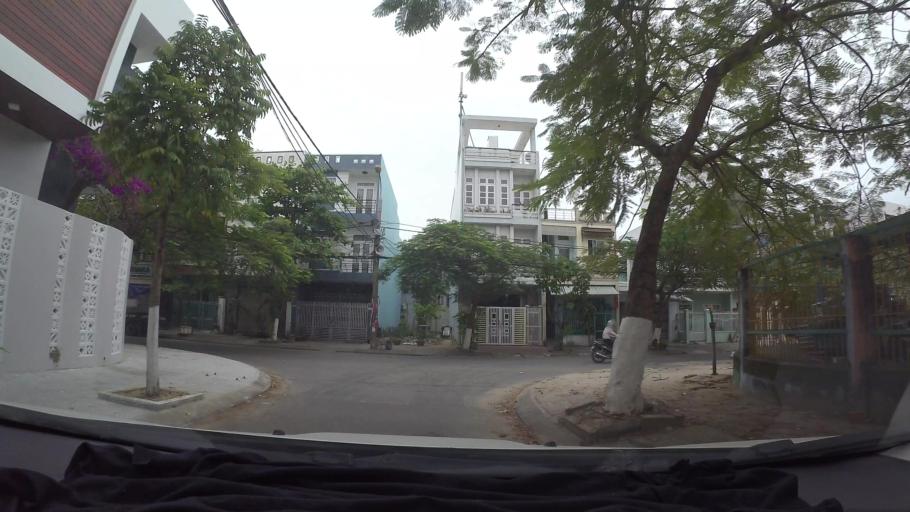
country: VN
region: Da Nang
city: Cam Le
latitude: 16.0308
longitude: 108.2285
